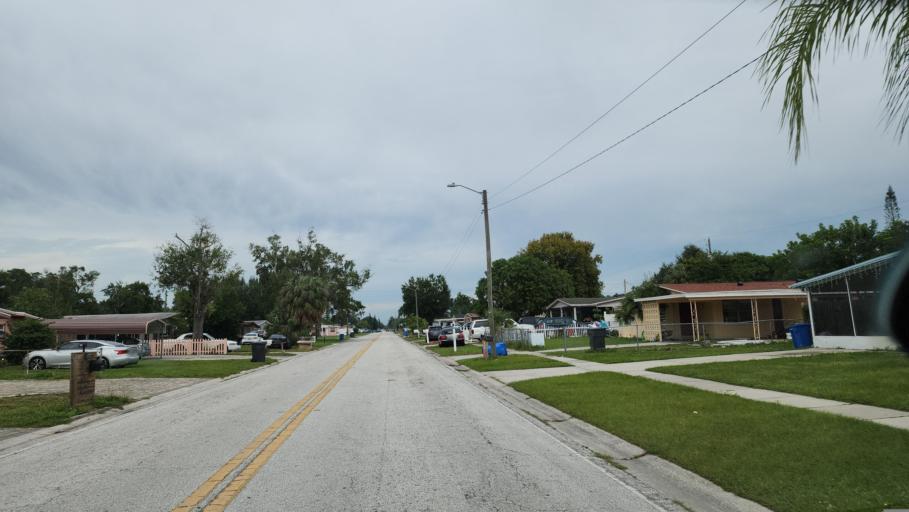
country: US
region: Florida
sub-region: Hillsborough County
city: Town 'n' Country
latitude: 27.9876
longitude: -82.5689
